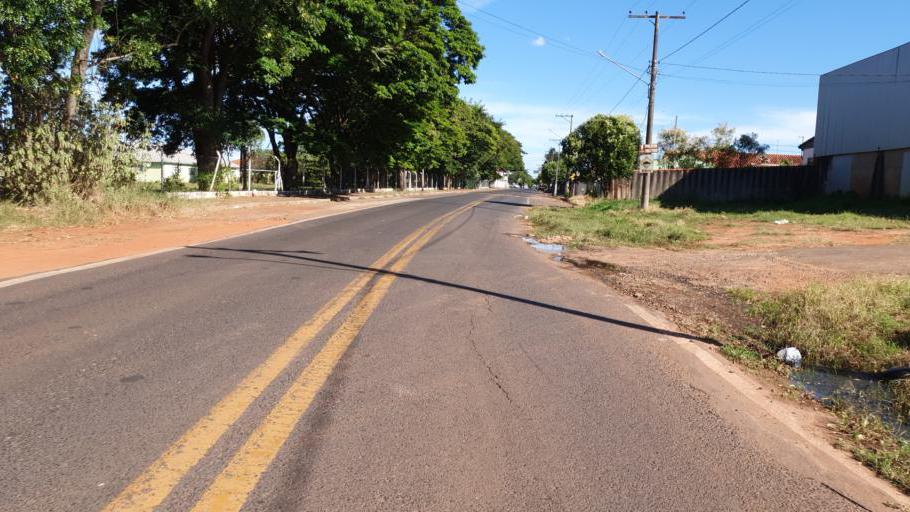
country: BR
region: Sao Paulo
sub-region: Paraguacu Paulista
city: Paraguacu Paulista
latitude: -22.4039
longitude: -50.5709
